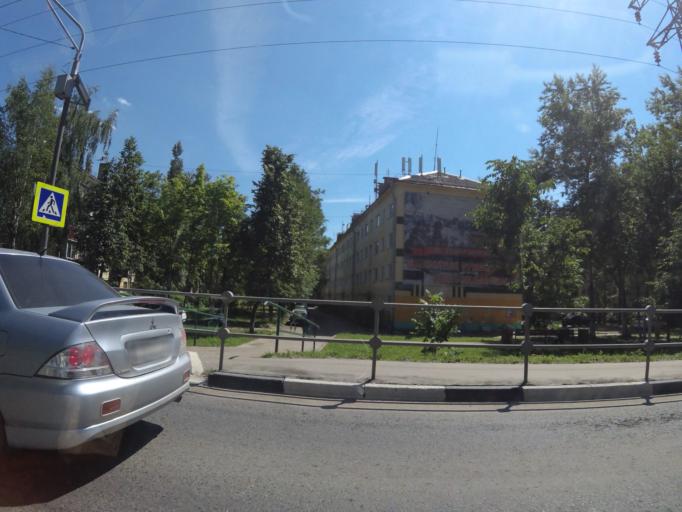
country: RU
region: Moskovskaya
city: Lobnya
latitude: 56.0102
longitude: 37.4650
